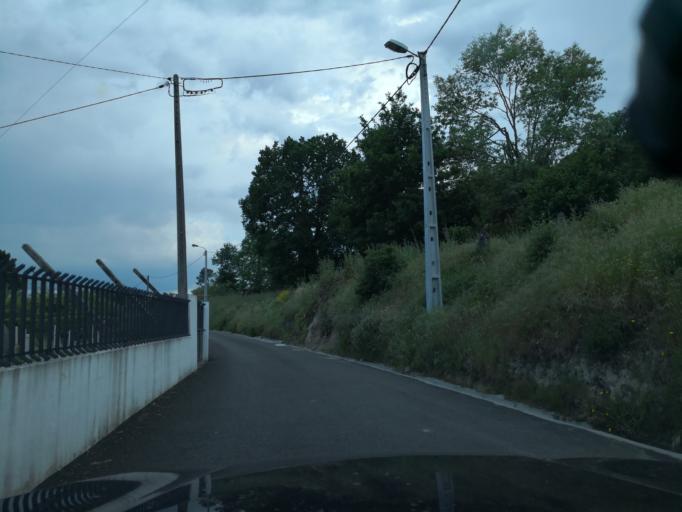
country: PT
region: Vila Real
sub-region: Vila Real
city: Vila Real
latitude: 41.3234
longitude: -7.7501
